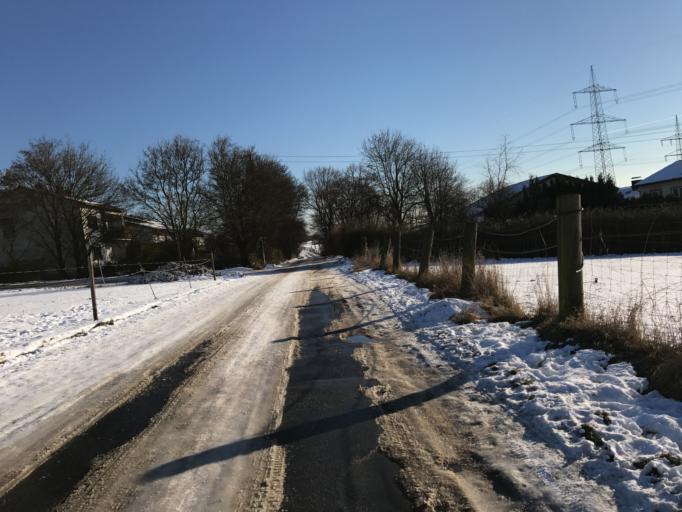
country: DE
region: Hesse
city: Eppstein
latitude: 50.0984
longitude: 8.4004
